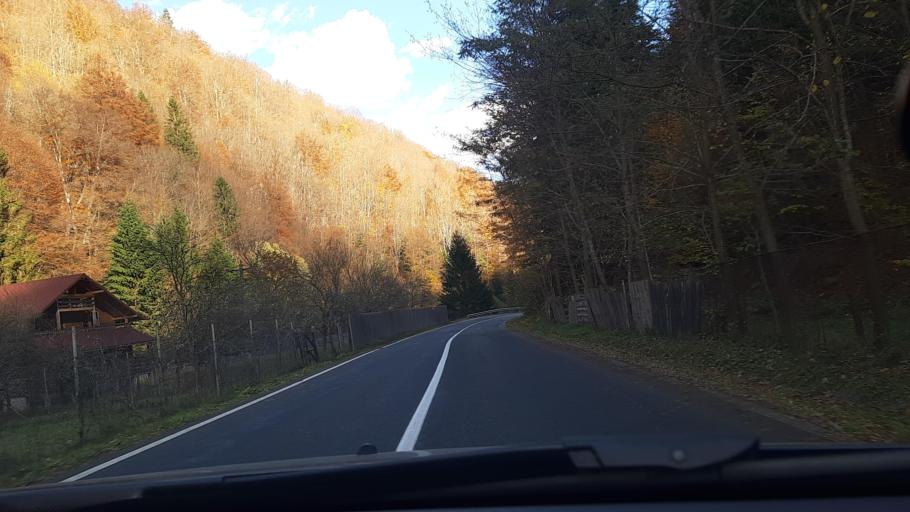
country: RO
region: Valcea
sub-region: Comuna Voineasa
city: Voineasa
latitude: 45.4240
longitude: 23.9396
